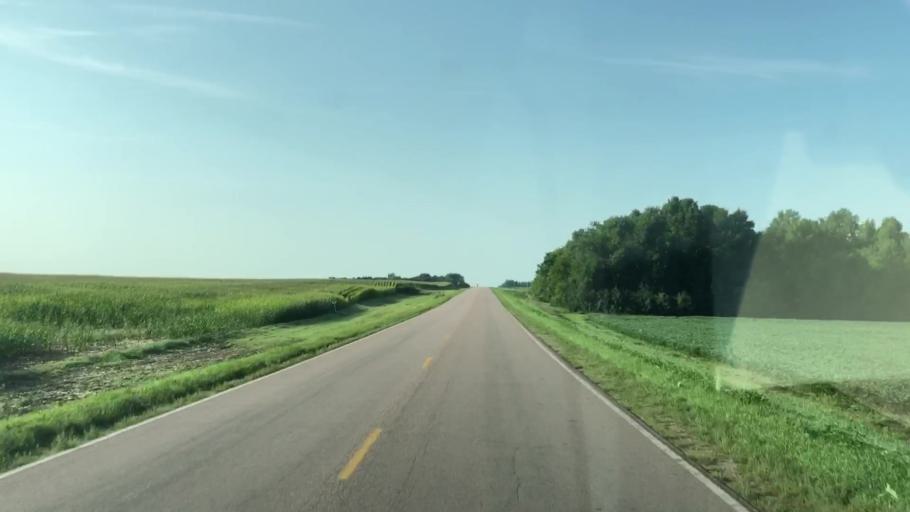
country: US
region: Iowa
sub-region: Lyon County
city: George
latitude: 43.3305
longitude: -95.9987
